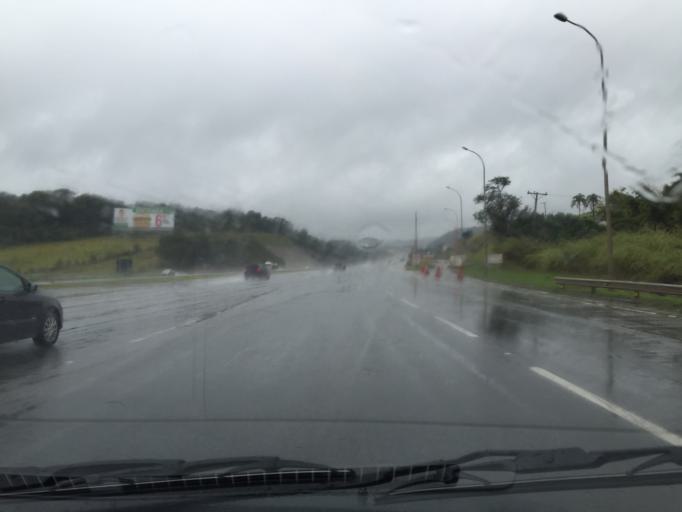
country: BR
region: Sao Paulo
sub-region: Itu
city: Itu
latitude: -23.4068
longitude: -47.2988
